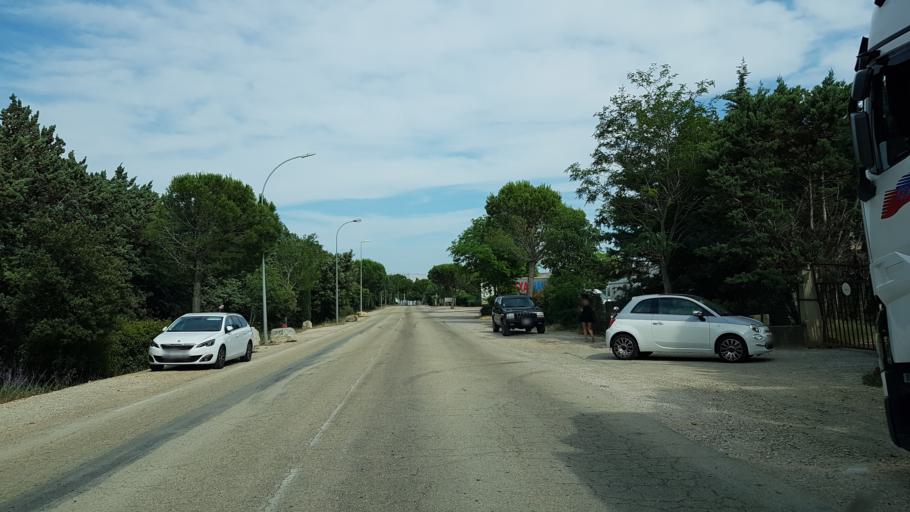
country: FR
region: Provence-Alpes-Cote d'Azur
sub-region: Departement des Bouches-du-Rhone
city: Saint-Martin-de-Crau
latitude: 43.6222
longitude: 4.7892
